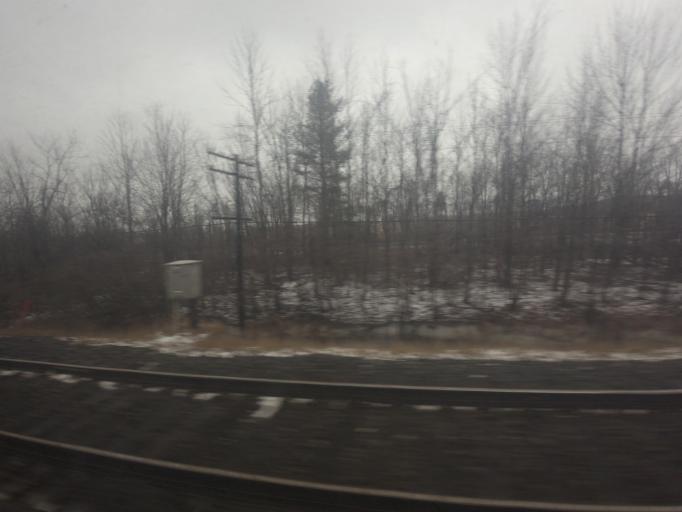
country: CA
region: Ontario
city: Quinte West
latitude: 44.0646
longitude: -77.6705
